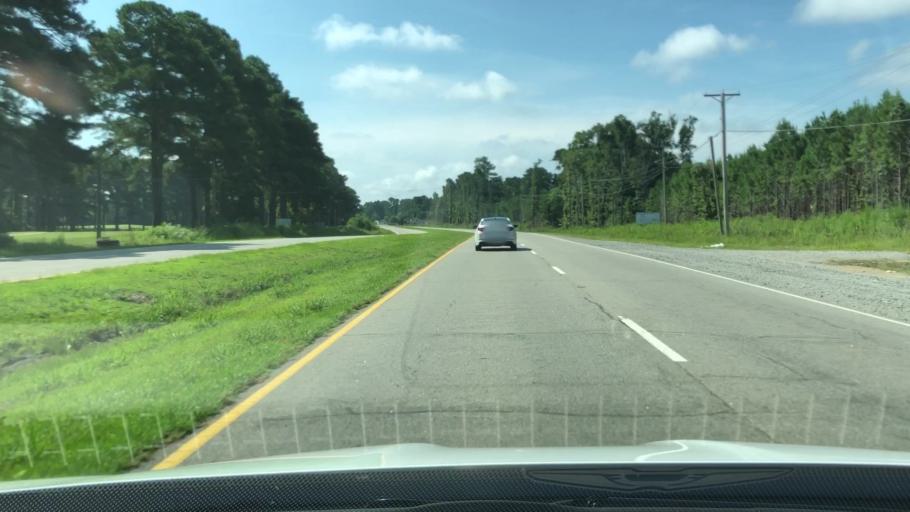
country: US
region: North Carolina
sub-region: Bertie County
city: Windsor
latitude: 35.9748
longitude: -76.9560
